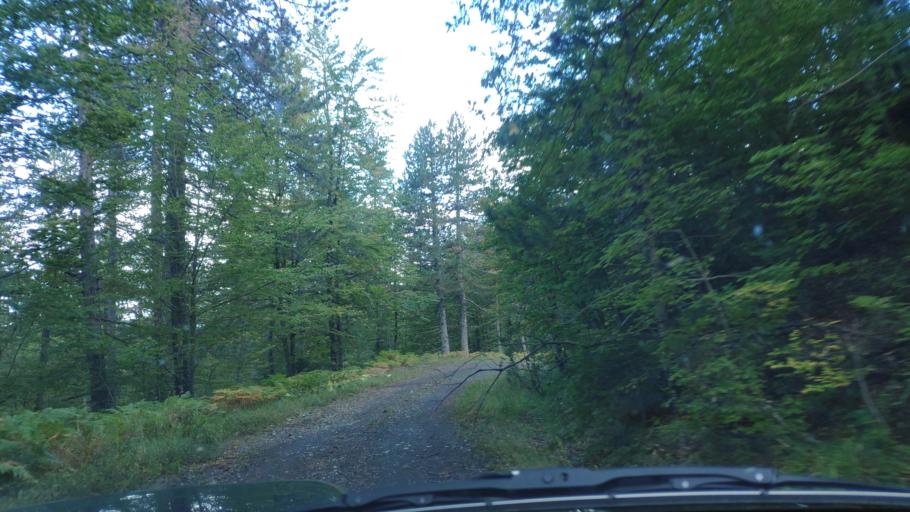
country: AL
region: Korce
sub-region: Rrethi i Devollit
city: Miras
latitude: 40.3454
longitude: 20.8994
